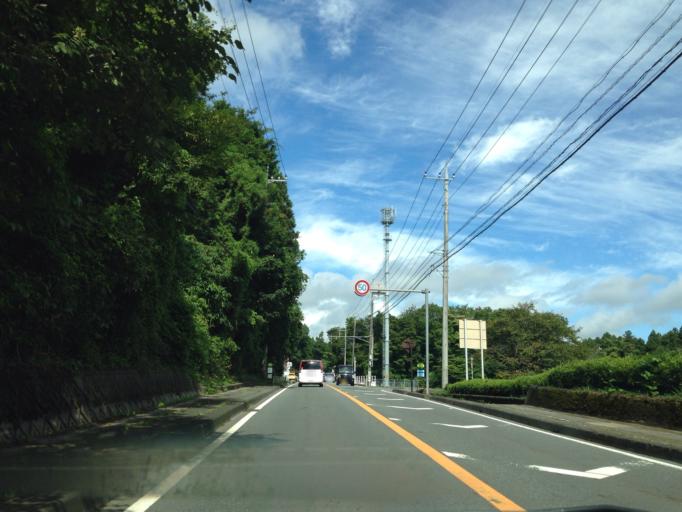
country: JP
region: Shizuoka
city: Gotemba
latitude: 35.3309
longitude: 138.9041
